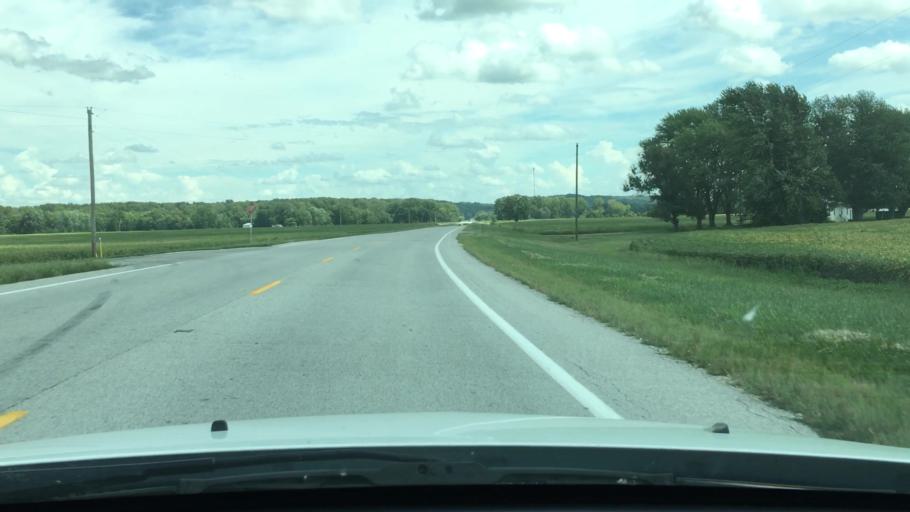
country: US
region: Missouri
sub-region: Pike County
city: Louisiana
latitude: 39.4987
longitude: -90.9993
